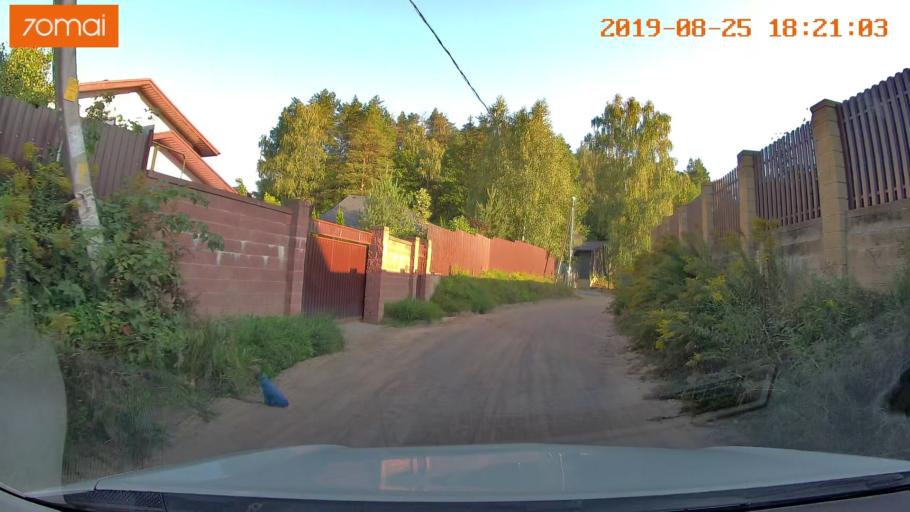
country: BY
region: Minsk
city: Khatsyezhyna
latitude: 53.9419
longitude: 27.3076
